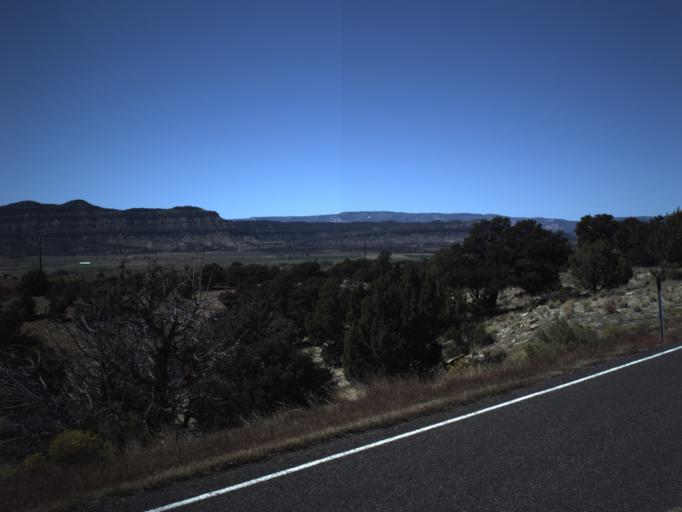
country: US
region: Utah
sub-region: Wayne County
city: Loa
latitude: 37.7360
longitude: -111.5443
